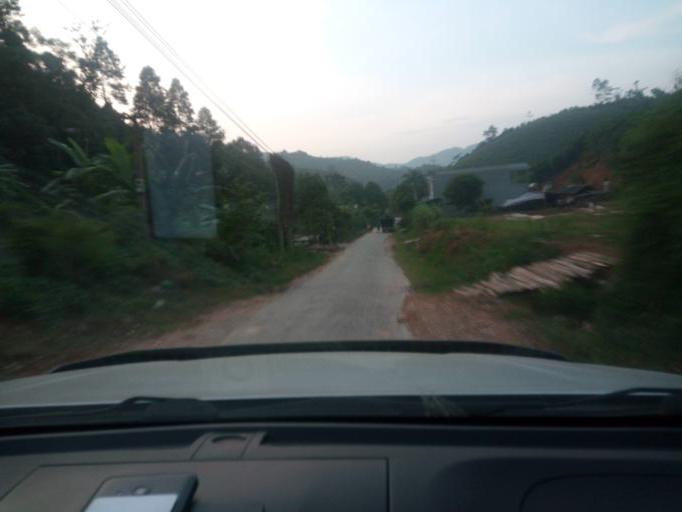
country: VN
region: Yen Bai
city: Co Phuc
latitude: 21.8391
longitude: 104.6171
